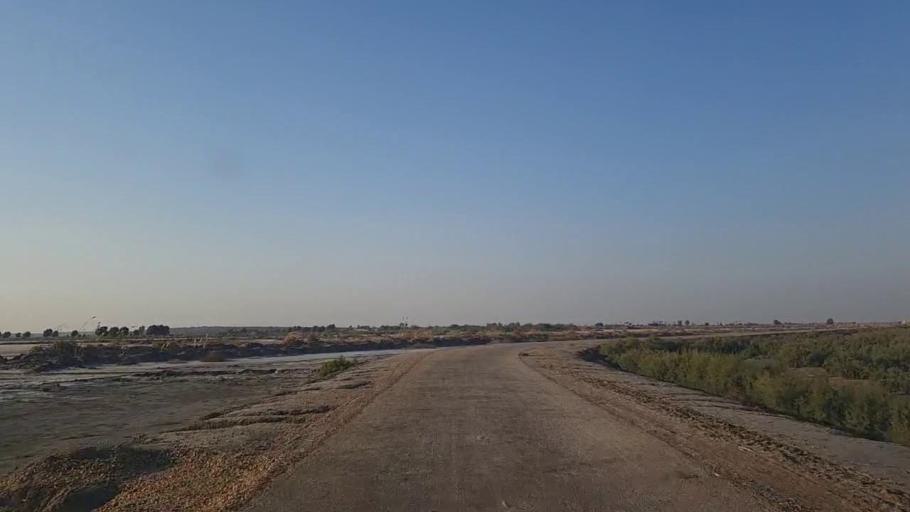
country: PK
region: Sindh
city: Jam Sahib
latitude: 26.3259
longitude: 68.6668
